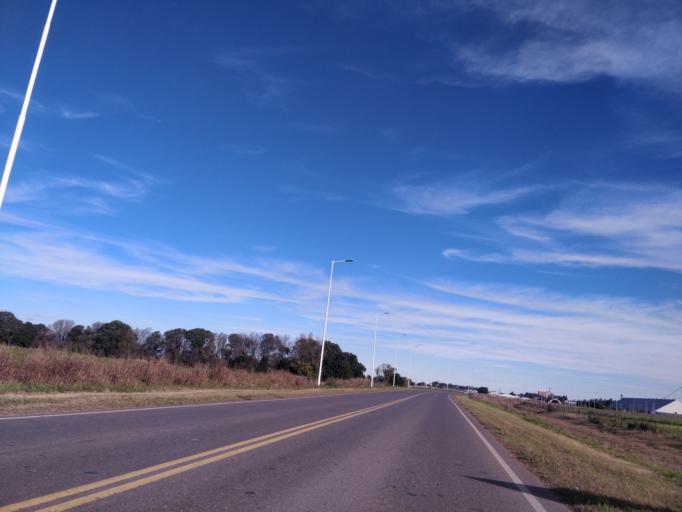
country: AR
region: Cordoba
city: Leones
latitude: -32.6449
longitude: -62.2910
